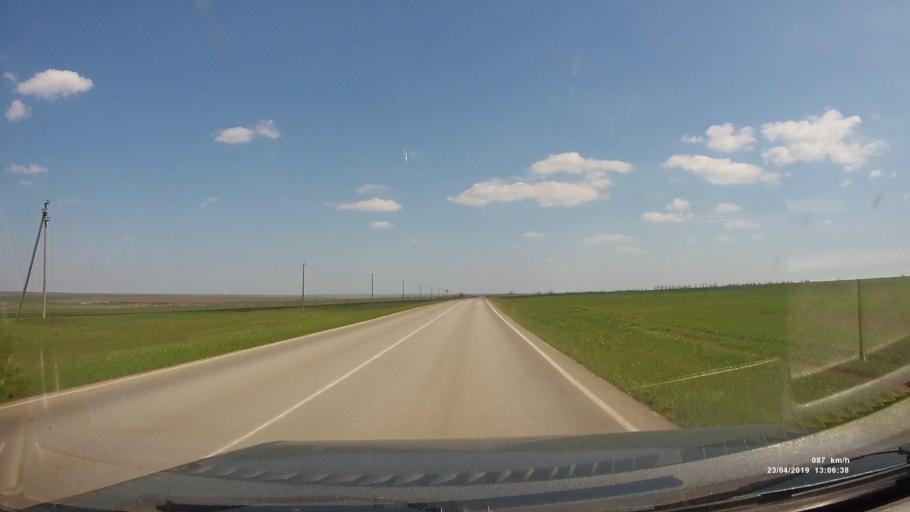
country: RU
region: Kalmykiya
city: Yashalta
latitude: 46.5918
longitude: 42.7450
